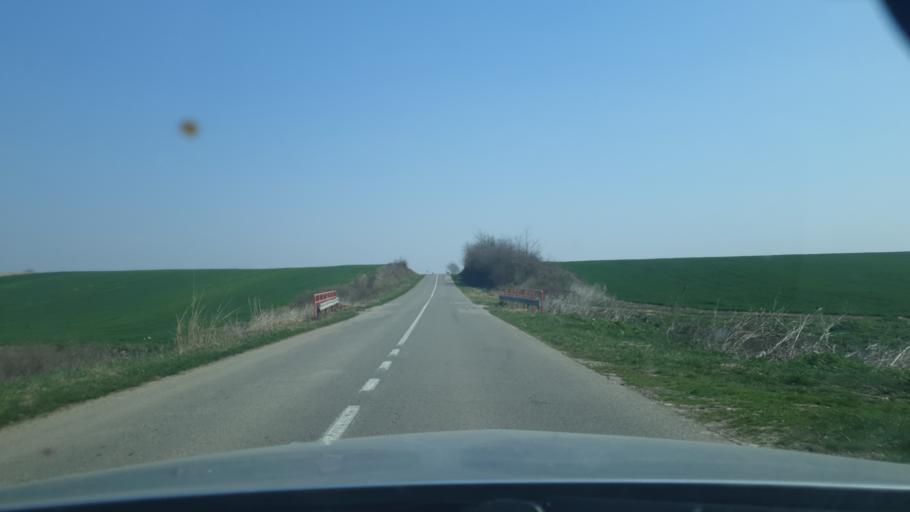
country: RS
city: Sasinci
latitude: 45.0479
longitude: 19.6962
